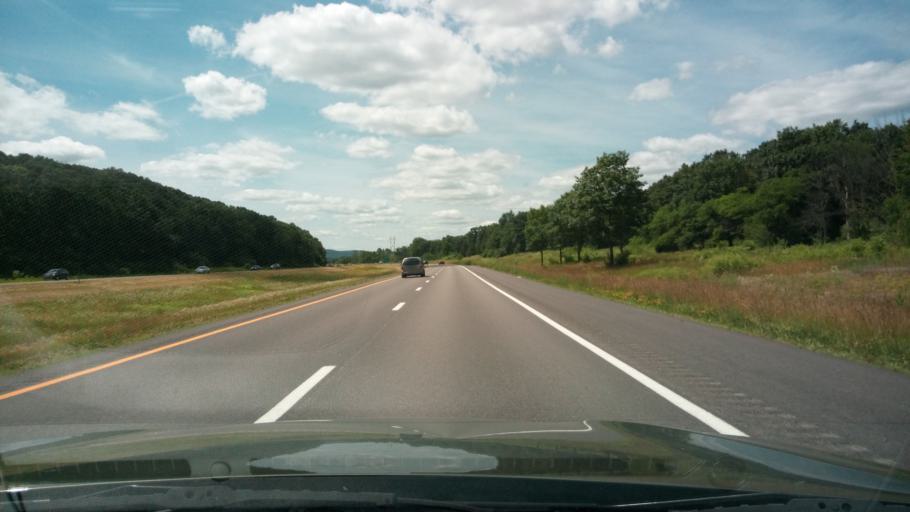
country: US
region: Pennsylvania
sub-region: Bradford County
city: South Waverly
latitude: 42.0202
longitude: -76.6506
